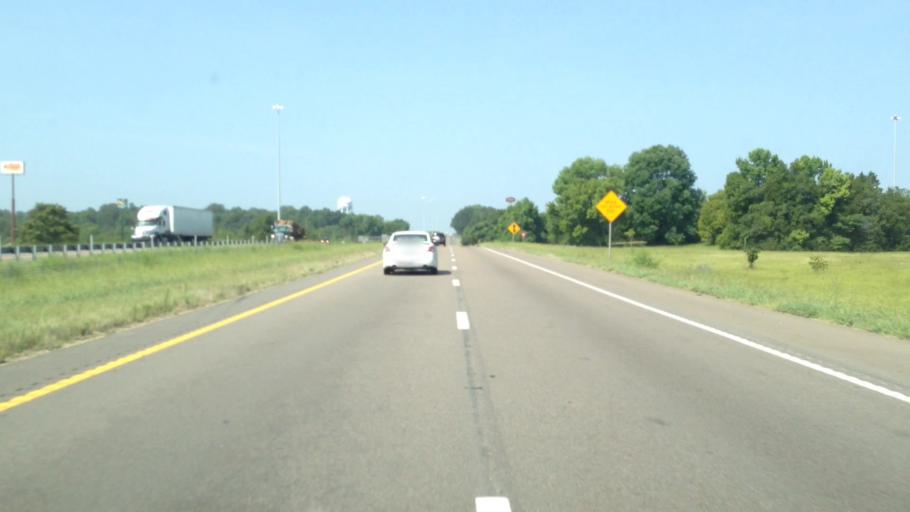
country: US
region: Mississippi
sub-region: Warren County
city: Beechwood
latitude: 32.3450
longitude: -90.8408
